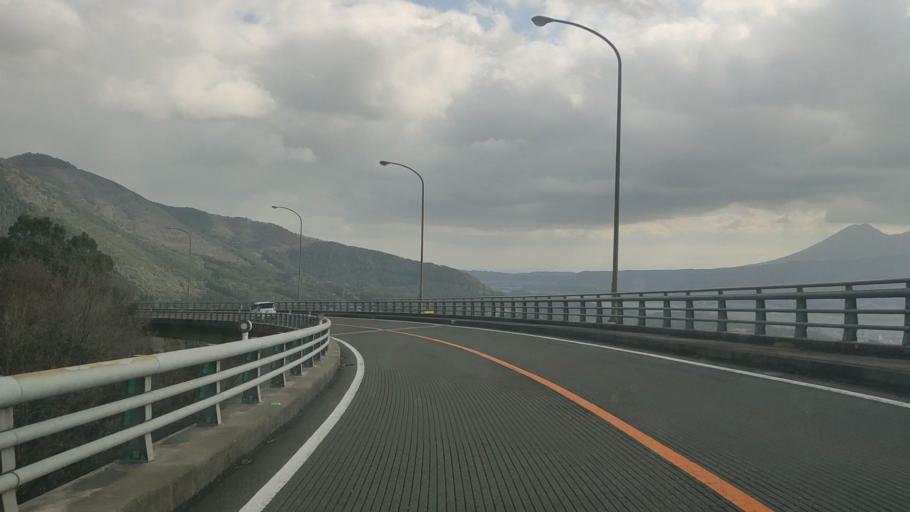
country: JP
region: Kumamoto
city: Hitoyoshi
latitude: 32.0730
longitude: 130.7996
